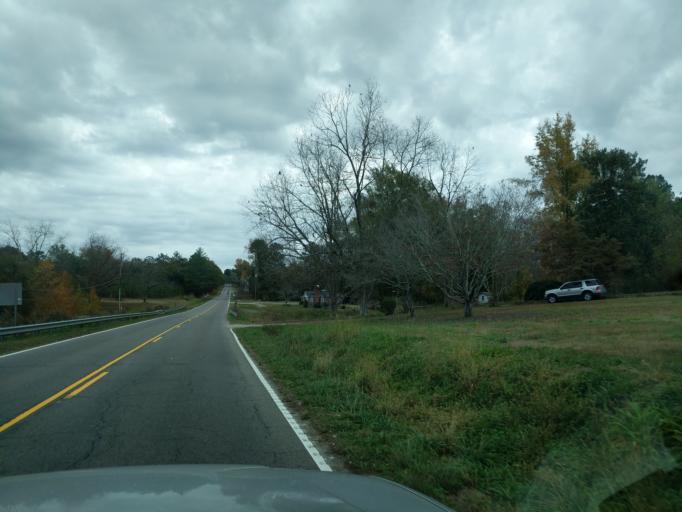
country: US
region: South Carolina
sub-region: Lexington County
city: Batesburg
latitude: 33.9173
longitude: -81.5700
